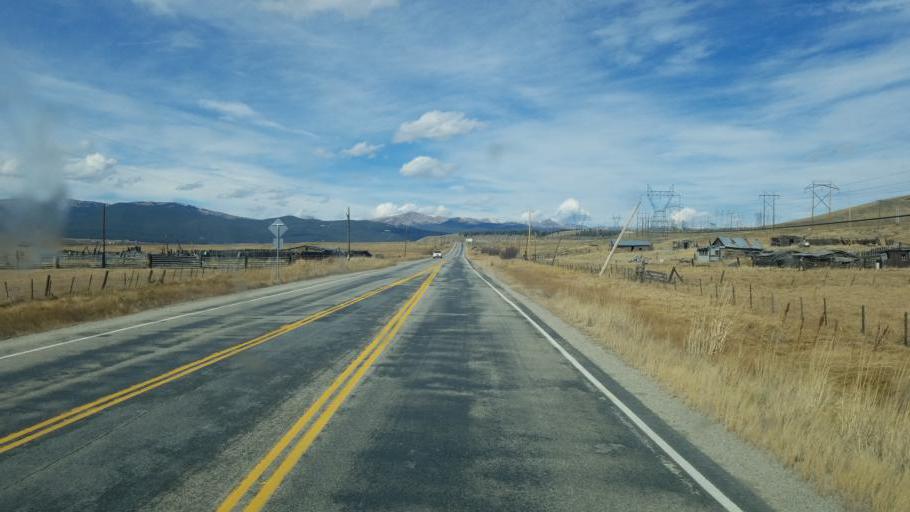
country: US
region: Colorado
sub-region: Lake County
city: Leadville
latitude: 39.1774
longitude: -106.3240
